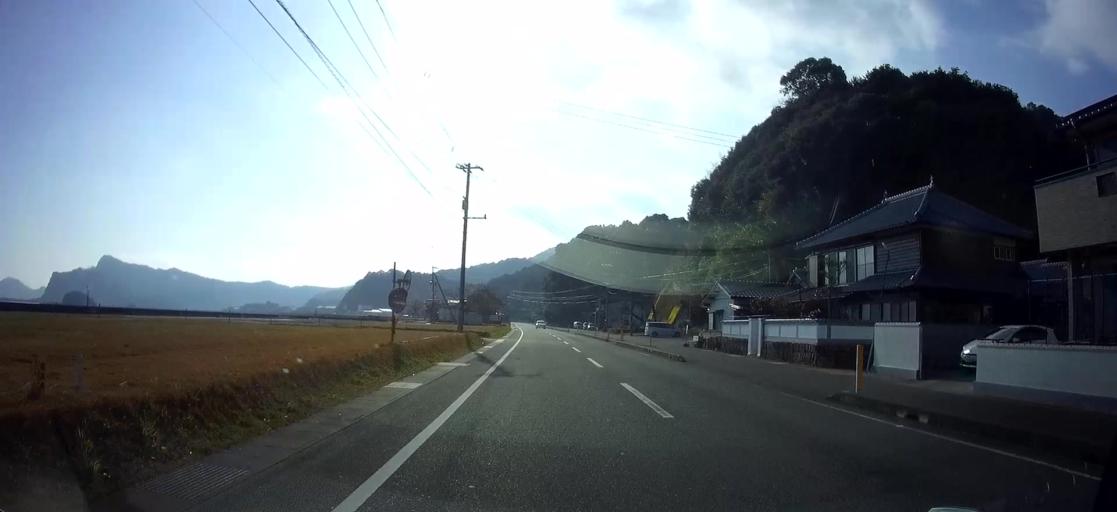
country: JP
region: Kumamoto
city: Yatsushiro
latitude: 32.4511
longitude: 130.4195
